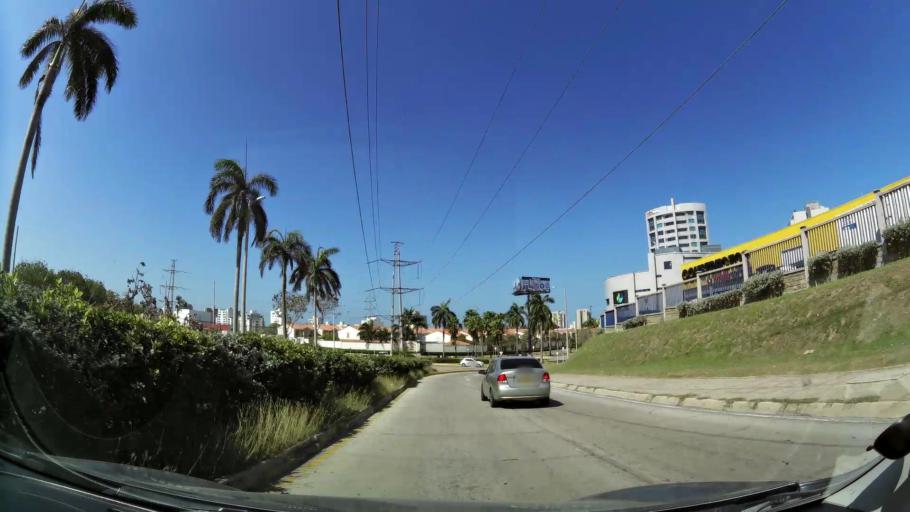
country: CO
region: Atlantico
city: Barranquilla
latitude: 11.0150
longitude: -74.8297
